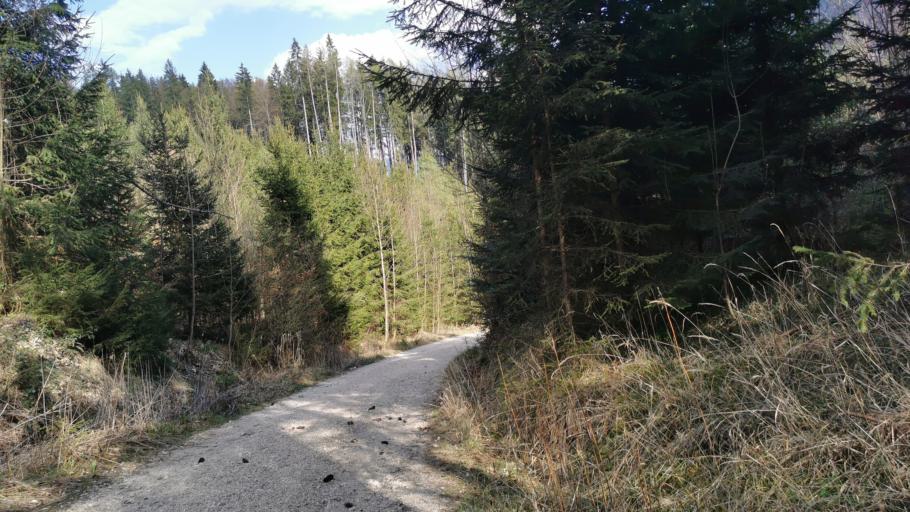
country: AT
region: Salzburg
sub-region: Politischer Bezirk Salzburg-Umgebung
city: Grodig
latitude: 47.7398
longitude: 12.9763
